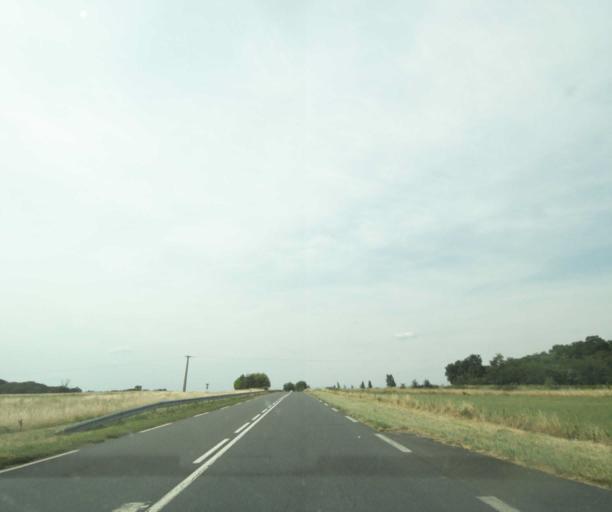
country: FR
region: Centre
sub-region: Departement d'Indre-et-Loire
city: Saint-Christophe-sur-le-Nais
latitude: 47.6333
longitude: 0.5020
